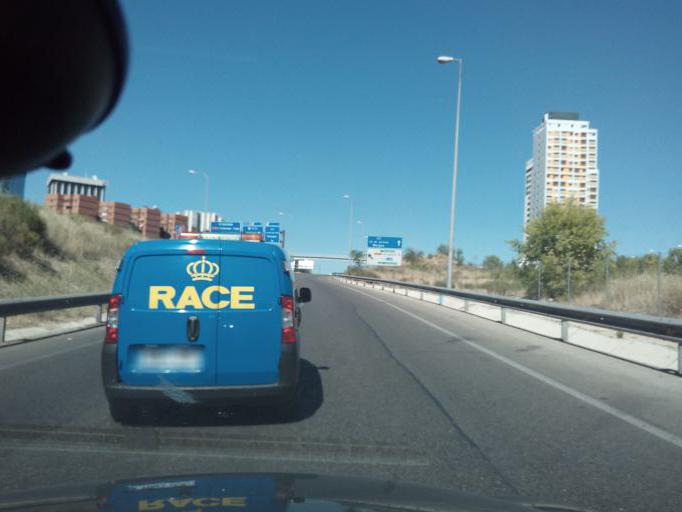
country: ES
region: Madrid
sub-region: Provincia de Madrid
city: Pinar de Chamartin
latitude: 40.4842
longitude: -3.6638
